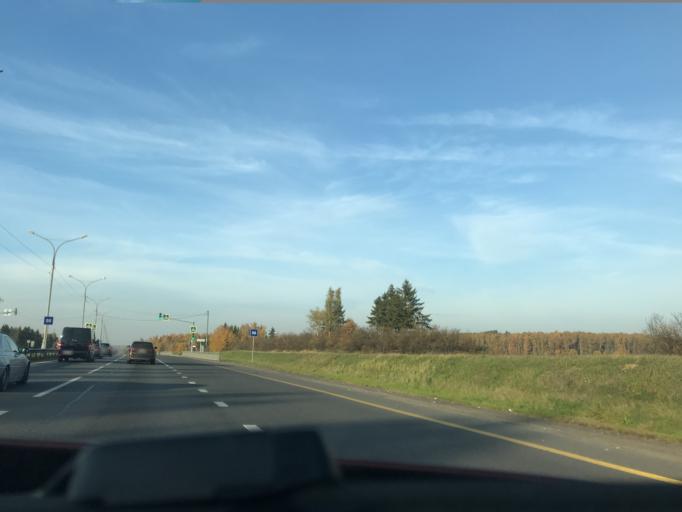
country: RU
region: Moskovskaya
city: Vostryakovo
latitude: 55.4707
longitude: 37.8536
